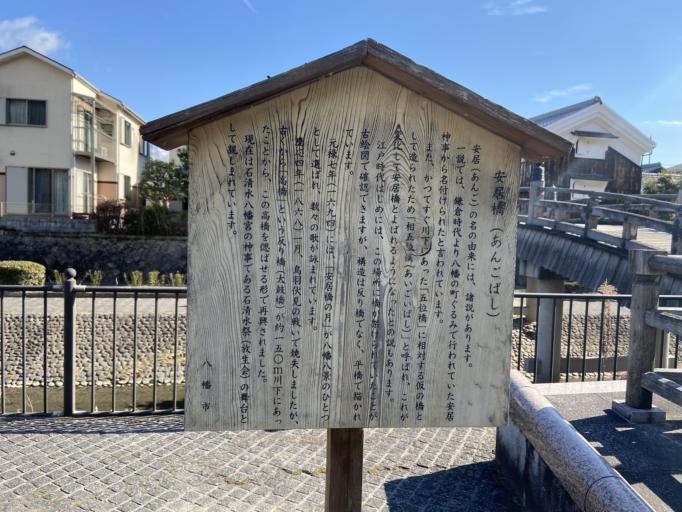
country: JP
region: Kyoto
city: Yawata
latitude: 34.8823
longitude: 135.7024
